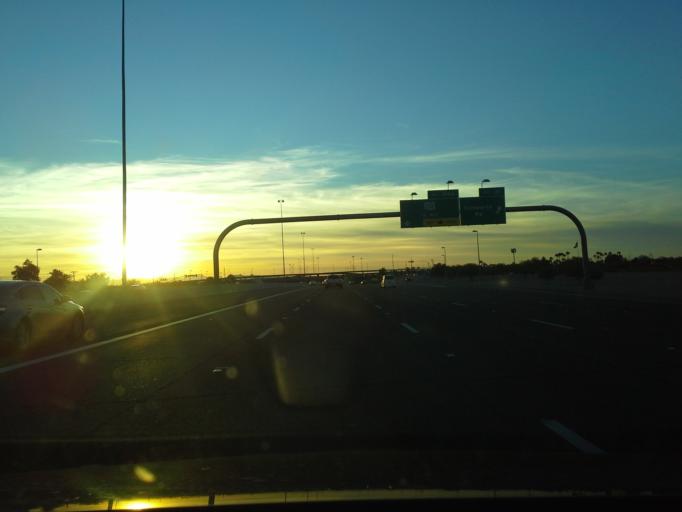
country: US
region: Arizona
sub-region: Pinal County
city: Apache Junction
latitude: 33.3867
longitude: -111.6267
